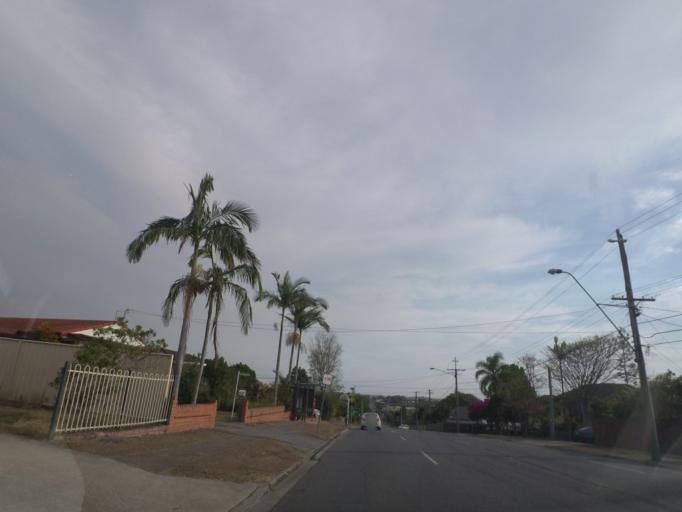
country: AU
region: Queensland
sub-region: Brisbane
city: Coopers Plains
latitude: -27.5548
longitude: 153.0412
